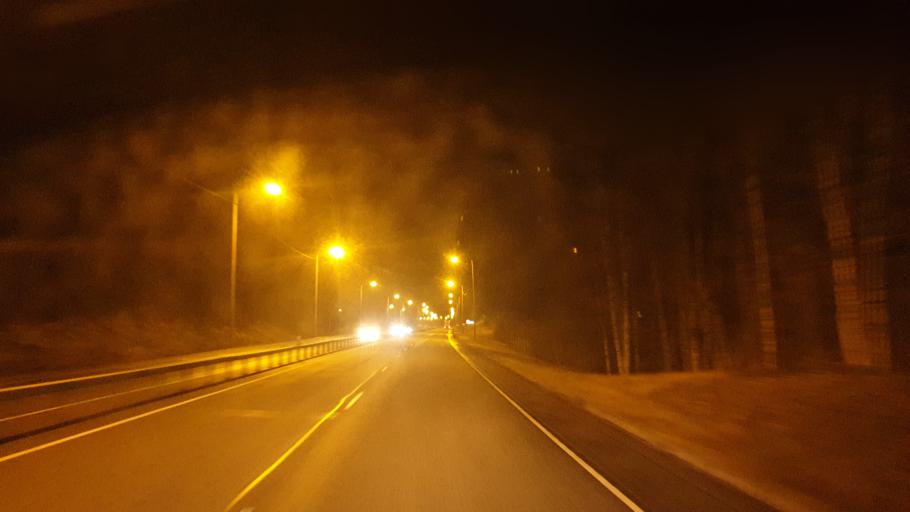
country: FI
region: Southern Savonia
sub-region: Mikkeli
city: Pertunmaa
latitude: 61.4341
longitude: 26.6541
